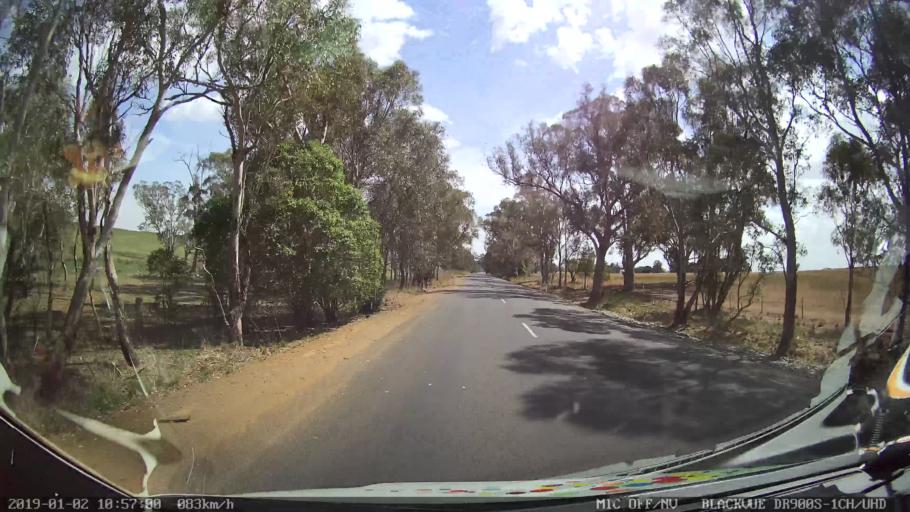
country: AU
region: New South Wales
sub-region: Cootamundra
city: Cootamundra
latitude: -34.6406
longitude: 148.2801
